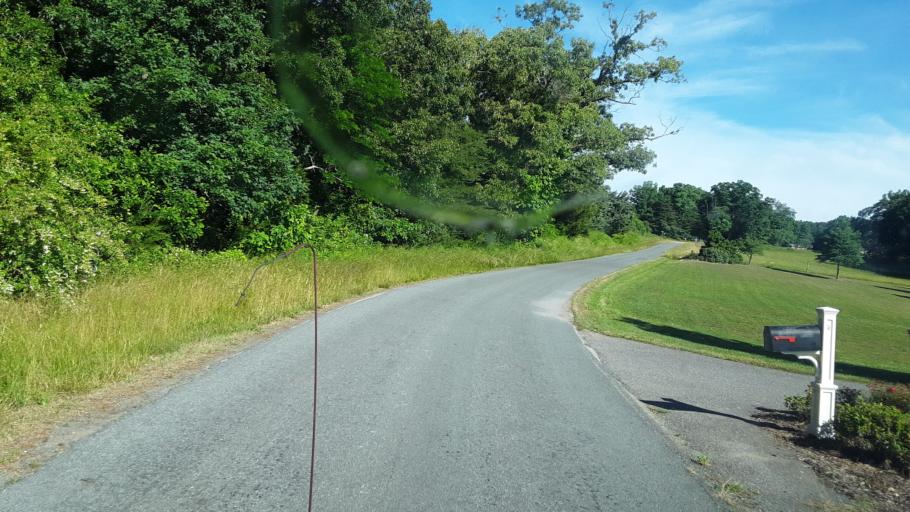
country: US
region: Virginia
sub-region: Pittsylvania County
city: Chatham
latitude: 36.8405
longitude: -79.4147
